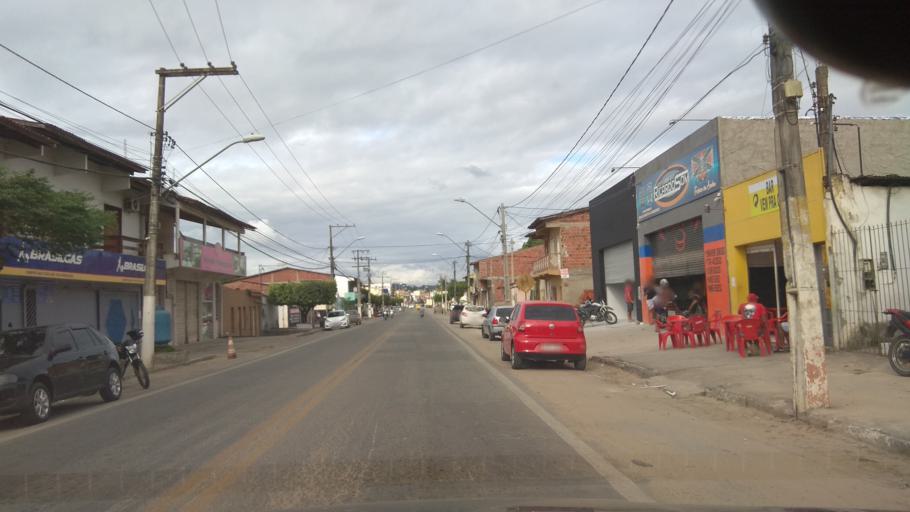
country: BR
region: Bahia
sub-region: Ipiau
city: Ipiau
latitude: -14.1346
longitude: -39.7486
